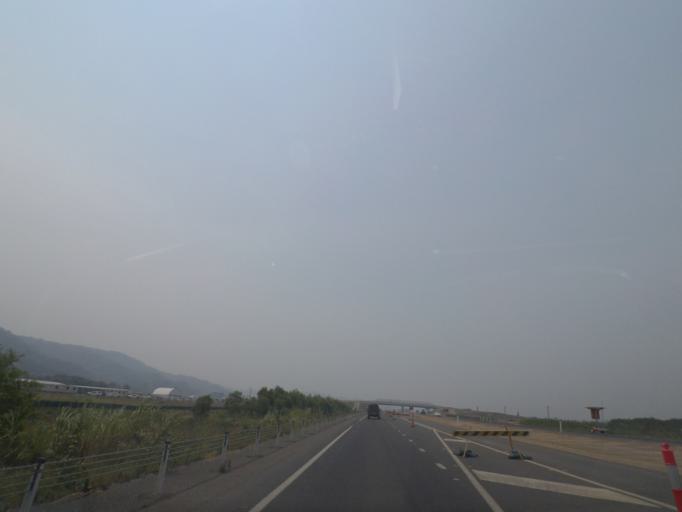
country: AU
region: New South Wales
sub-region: Ballina
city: Ballina
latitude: -28.9052
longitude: 153.4790
